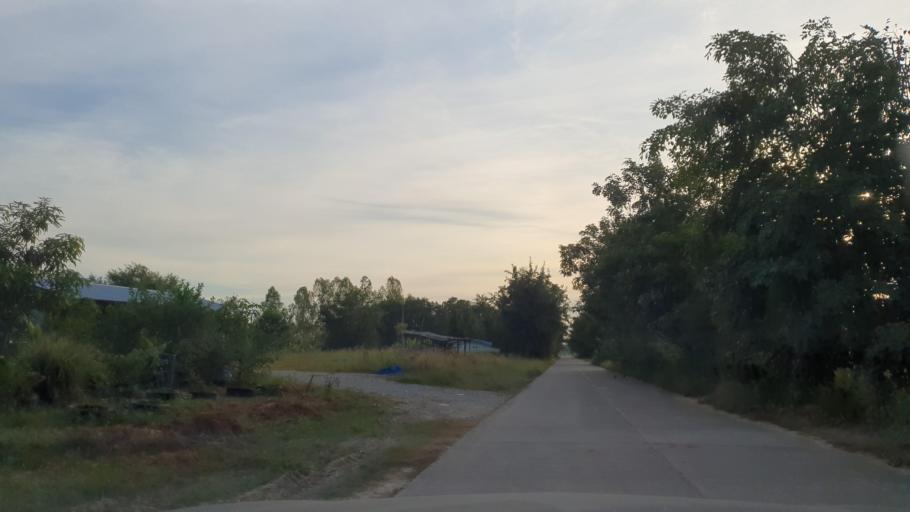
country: TH
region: Nakhon Sawan
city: Krok Phra
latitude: 15.6635
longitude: 100.0020
